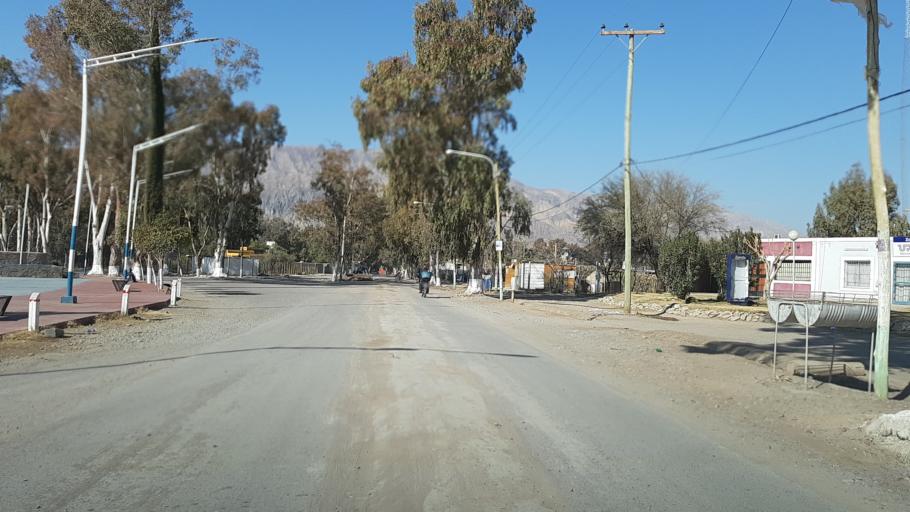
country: AR
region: San Juan
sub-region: Departamento de Zonda
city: Zonda
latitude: -31.5500
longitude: -68.7322
